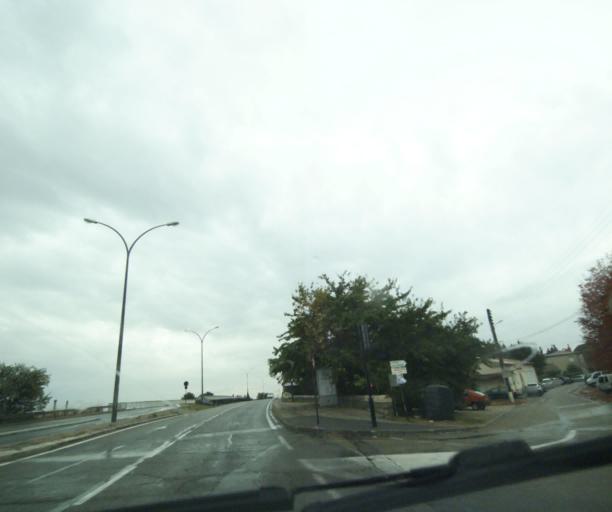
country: FR
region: Languedoc-Roussillon
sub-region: Departement du Gard
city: Rodilhan
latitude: 43.8490
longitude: 4.3994
